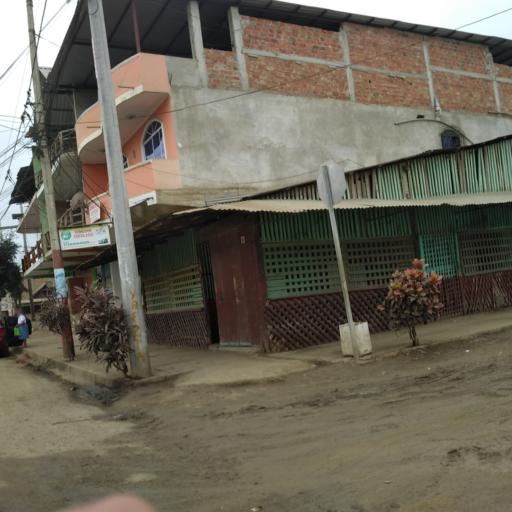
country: EC
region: Manabi
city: Jipijapa
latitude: -1.5612
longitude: -80.8125
